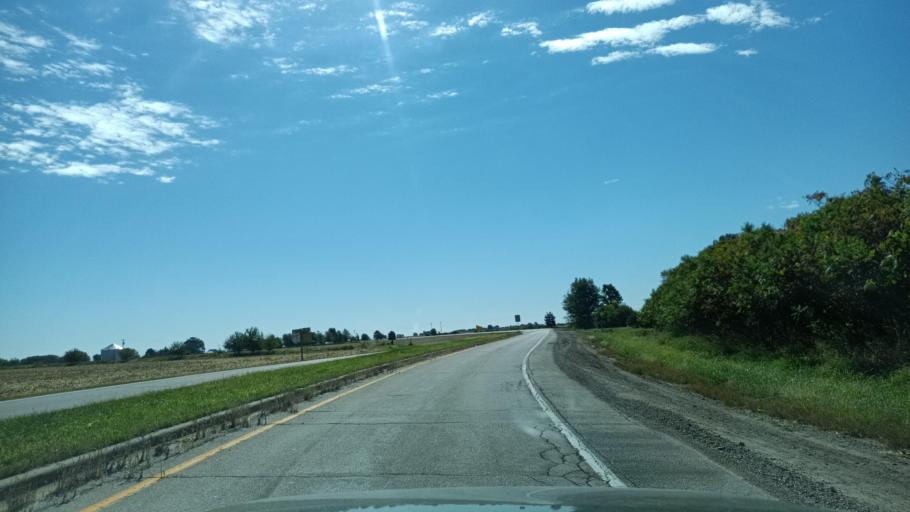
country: US
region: Illinois
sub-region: Knox County
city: Knoxville
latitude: 40.9121
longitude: -90.2459
